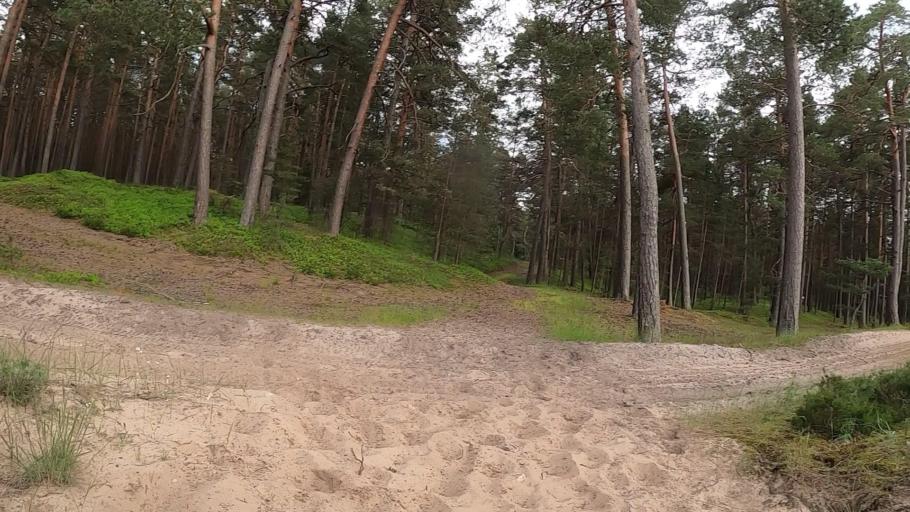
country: LV
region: Riga
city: Jaunciems
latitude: 57.0880
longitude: 24.1623
